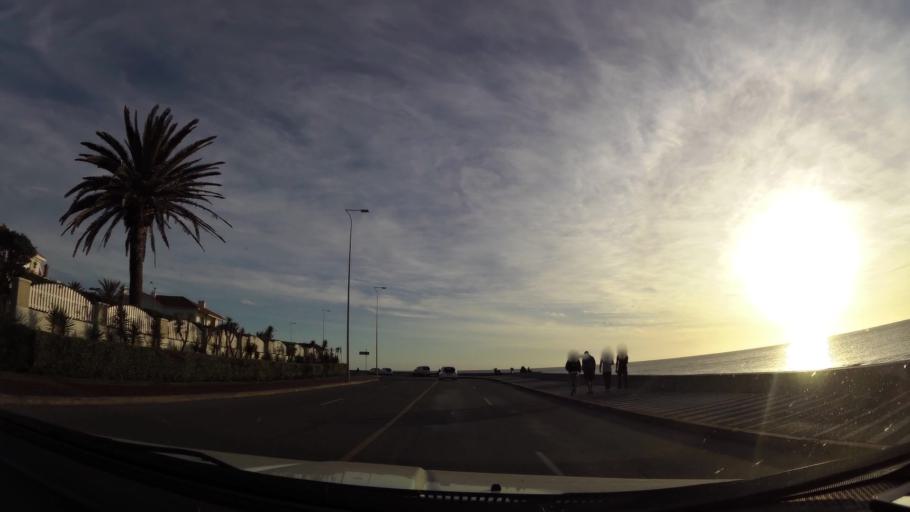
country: UY
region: Maldonado
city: Punta del Este
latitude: -34.9658
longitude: -54.9544
